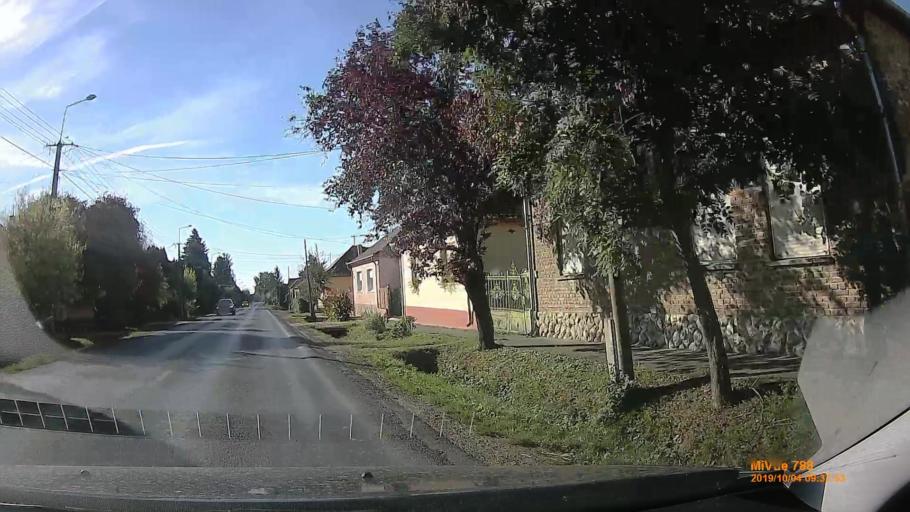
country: HU
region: Somogy
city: Kaposvar
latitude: 46.4637
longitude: 17.8046
